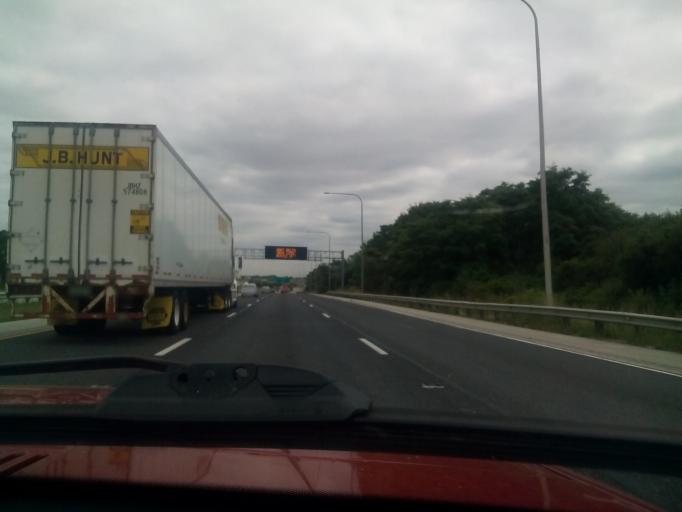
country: US
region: Illinois
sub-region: Cook County
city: Markham
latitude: 41.5830
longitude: -87.6936
